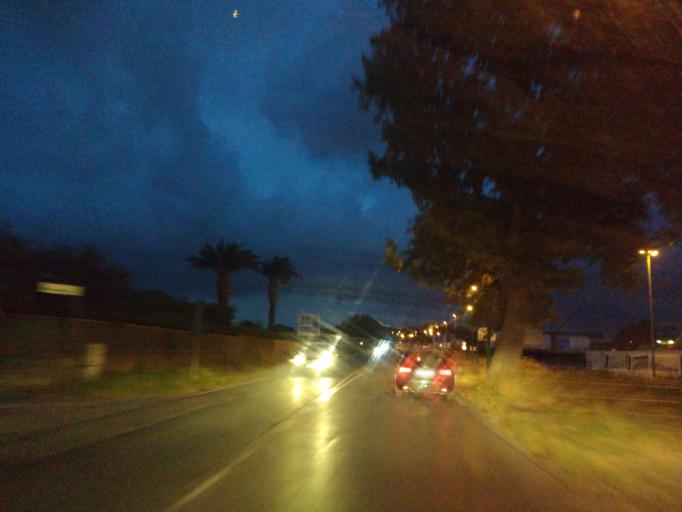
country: IT
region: Latium
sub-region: Citta metropolitana di Roma Capitale
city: Anzio
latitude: 41.4598
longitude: 12.6213
